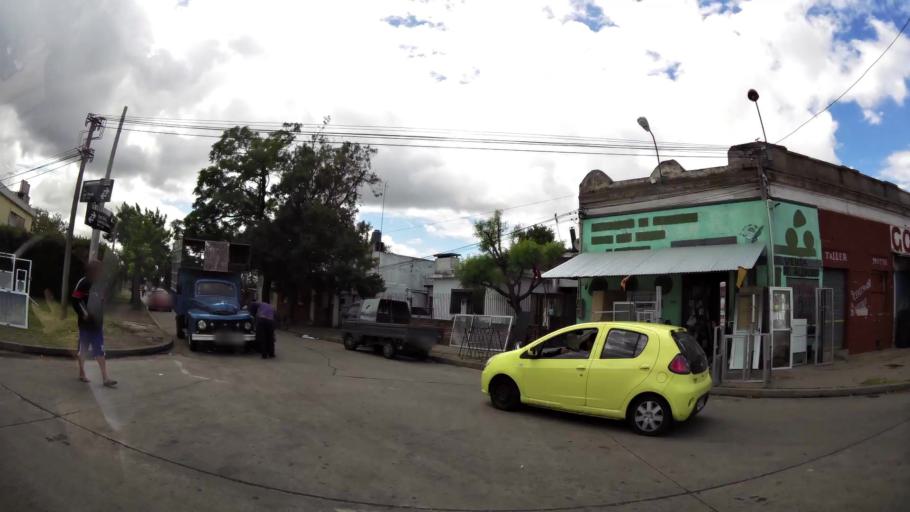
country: UY
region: Montevideo
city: Montevideo
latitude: -34.8300
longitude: -56.1419
